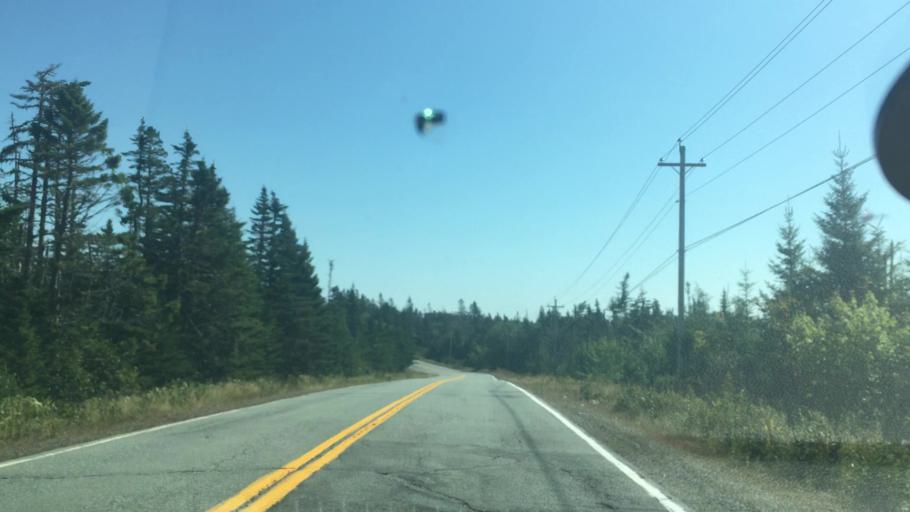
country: CA
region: Nova Scotia
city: New Glasgow
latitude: 44.9175
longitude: -62.3299
